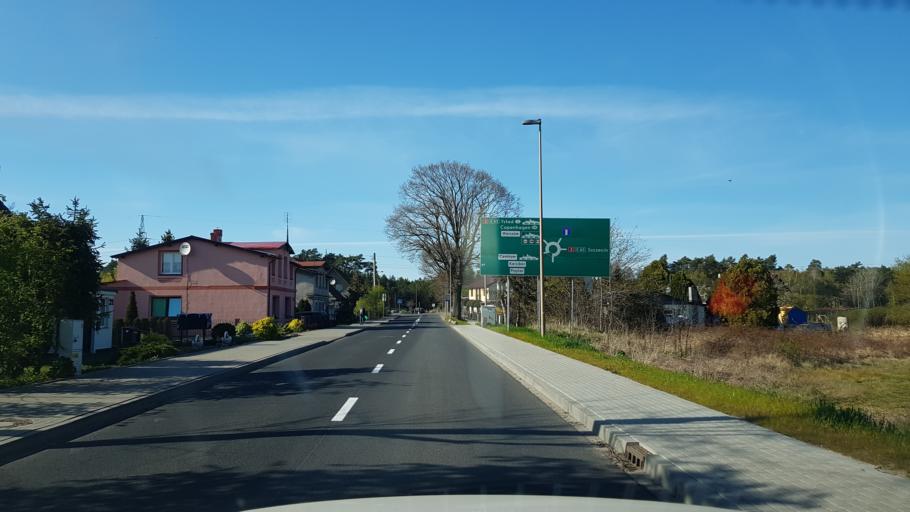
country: PL
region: West Pomeranian Voivodeship
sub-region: Powiat kamienski
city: Miedzyzdroje
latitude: 53.8942
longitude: 14.3578
